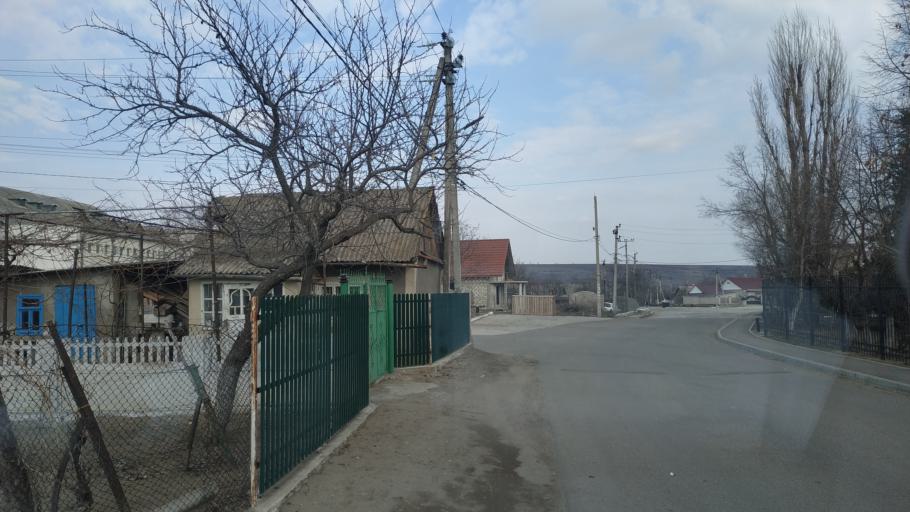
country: MD
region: Anenii Noi
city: Anenii Noi
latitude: 46.9010
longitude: 29.1383
